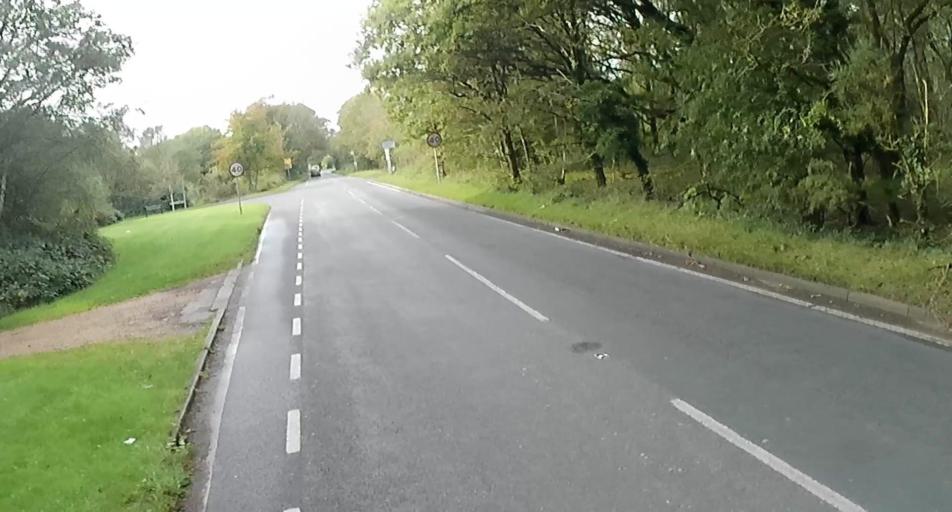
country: GB
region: England
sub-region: West Berkshire
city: Thatcham
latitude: 51.3773
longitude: -1.2452
